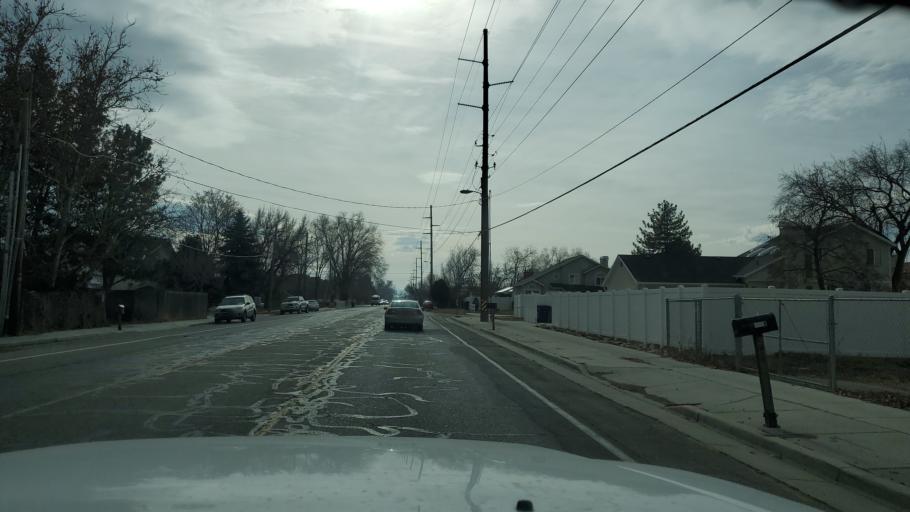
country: US
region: Utah
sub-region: Salt Lake County
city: Millcreek
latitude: 40.6815
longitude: -111.8656
